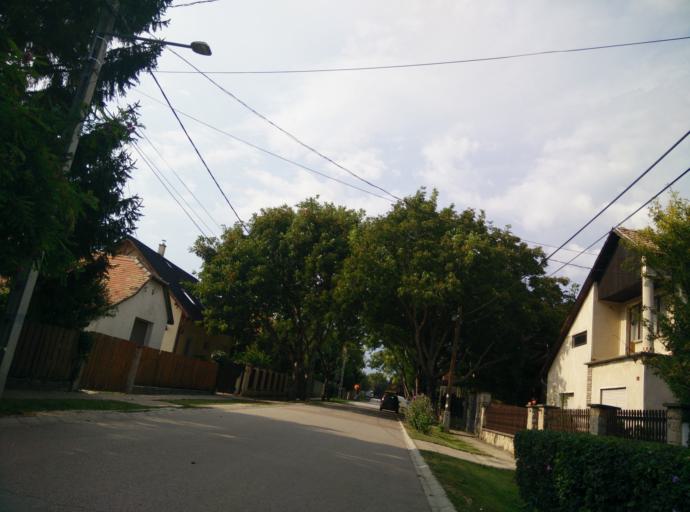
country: HU
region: Pest
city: Paty
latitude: 47.5159
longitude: 18.8258
